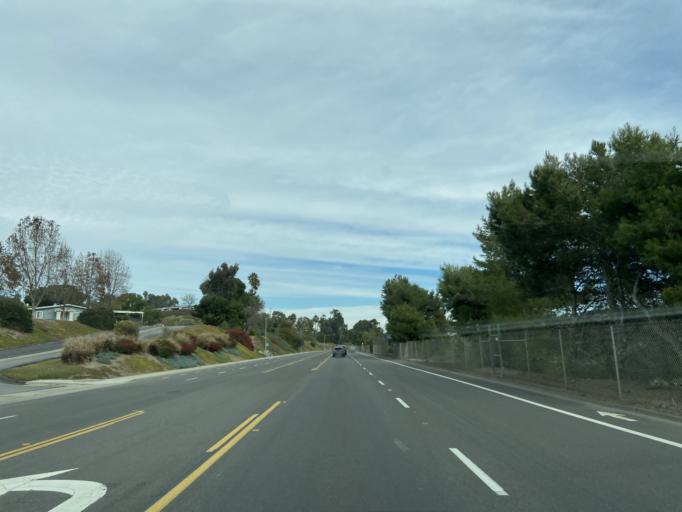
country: US
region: California
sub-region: San Diego County
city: Oceanside
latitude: 33.2100
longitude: -117.3273
